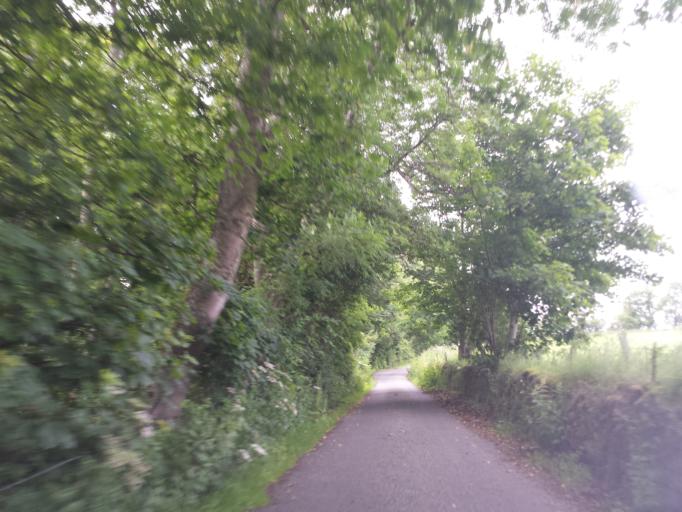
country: GB
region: Scotland
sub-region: Highland
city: Fortrose
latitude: 57.5059
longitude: -4.0084
